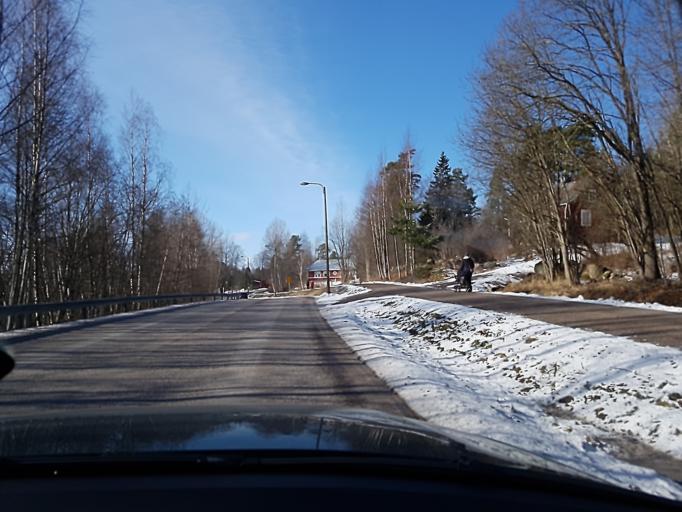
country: FI
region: Uusimaa
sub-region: Helsinki
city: Kirkkonummi
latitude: 60.1227
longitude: 24.4162
